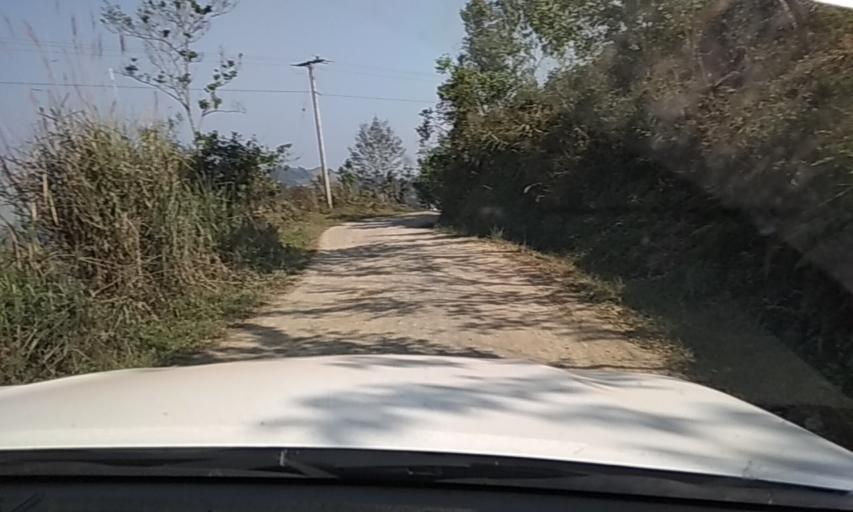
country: LA
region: Phongsali
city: Phongsali
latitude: 21.6528
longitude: 102.0918
